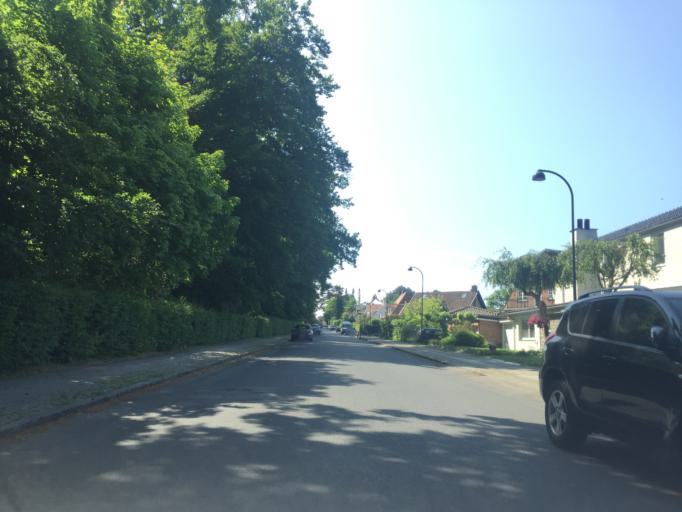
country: DK
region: Capital Region
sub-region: Lyngby-Tarbaek Kommune
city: Kongens Lyngby
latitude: 55.7577
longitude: 12.5443
